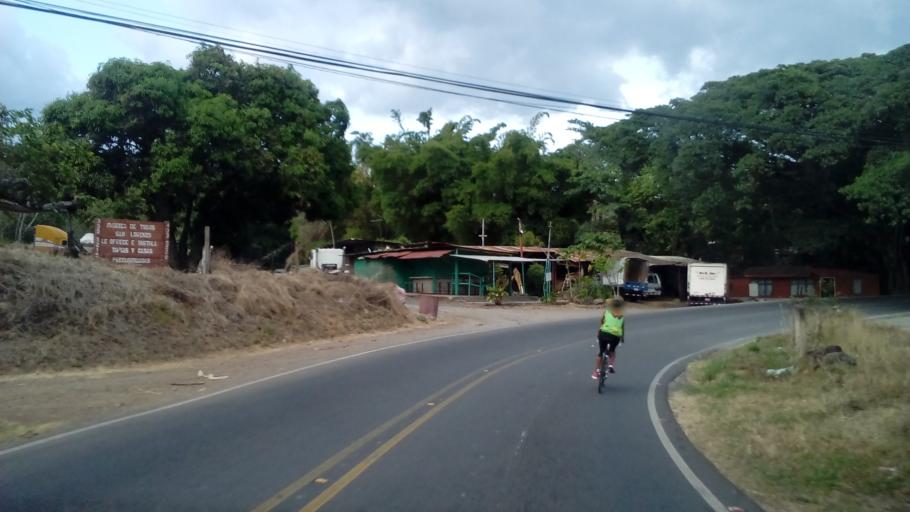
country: CR
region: Alajuela
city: Carrillos
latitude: 10.0399
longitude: -84.2433
